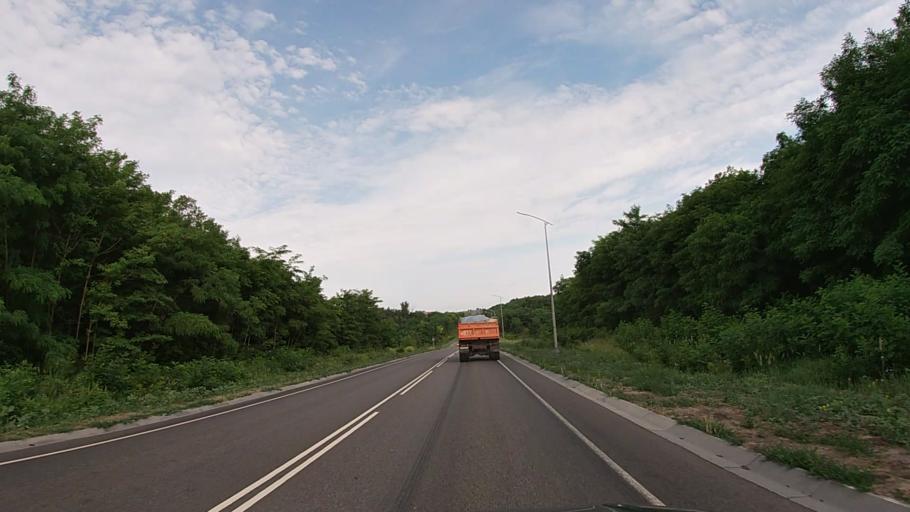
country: RU
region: Belgorod
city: Severnyy
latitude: 50.6674
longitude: 36.4929
